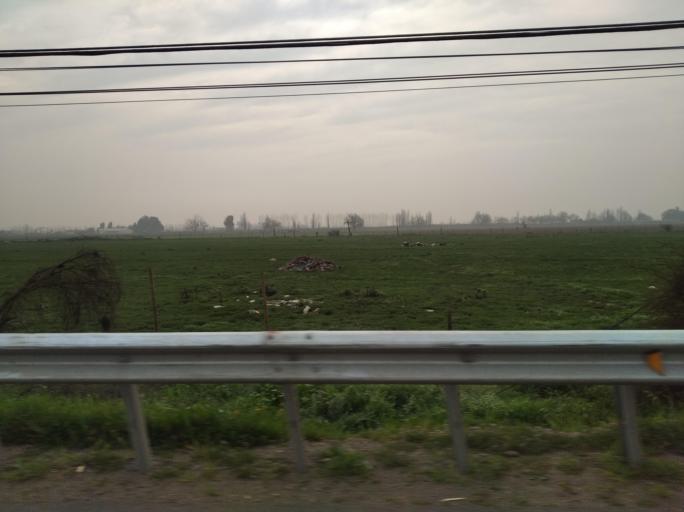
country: CL
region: Santiago Metropolitan
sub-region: Provincia de Chacabuco
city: Lampa
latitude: -33.3357
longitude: -70.8175
